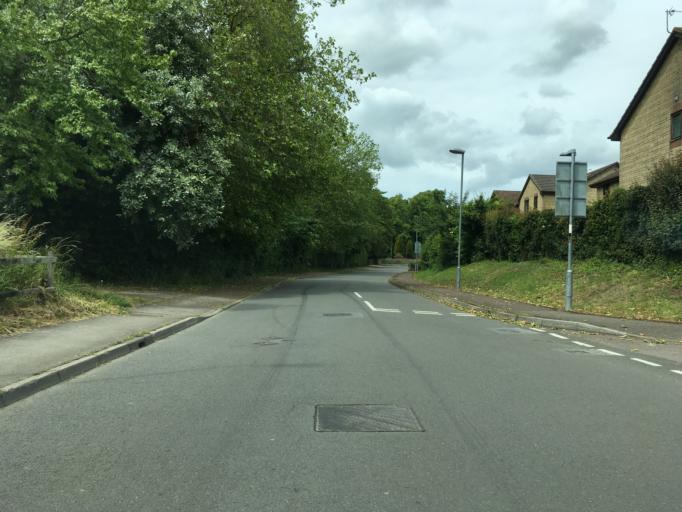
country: GB
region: England
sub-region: Wiltshire
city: Purton
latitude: 51.5716
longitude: -1.8641
